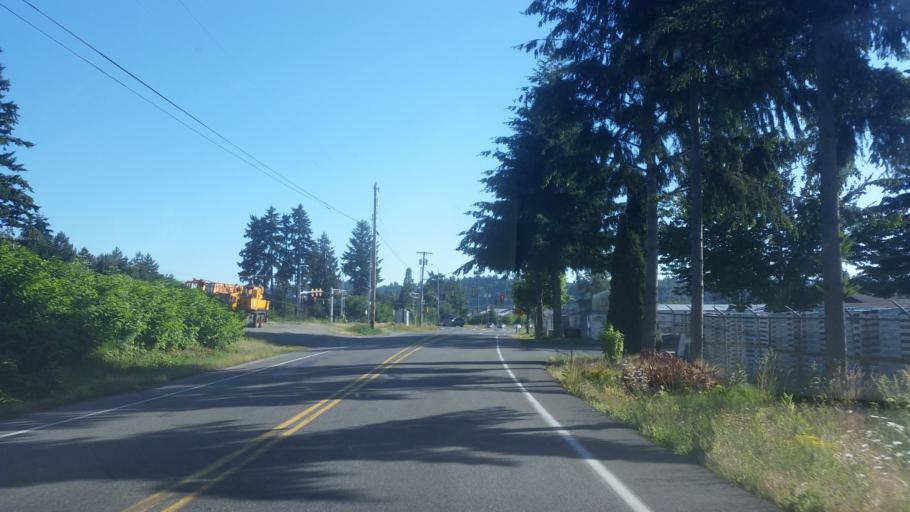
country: US
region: Washington
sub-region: King County
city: Woodinville
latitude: 47.7601
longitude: -122.1559
